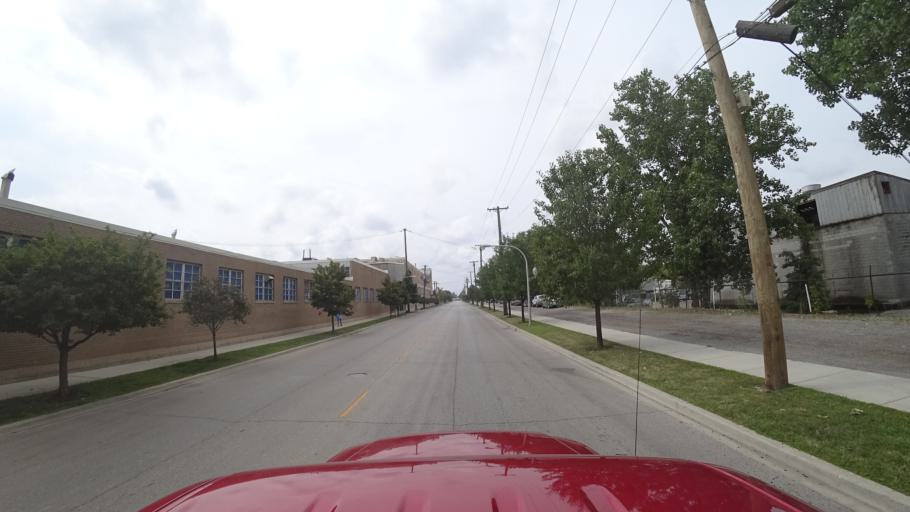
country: US
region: Illinois
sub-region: Cook County
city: Chicago
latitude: 41.8295
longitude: -87.6557
